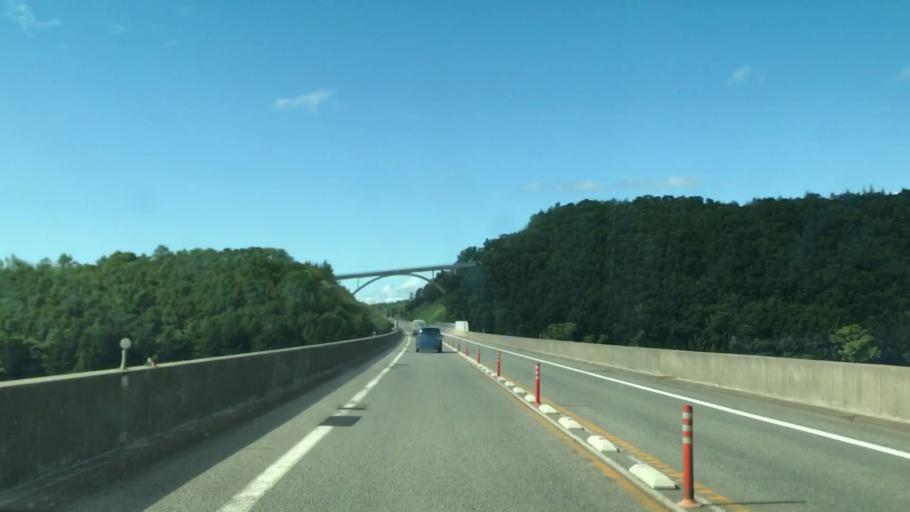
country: JP
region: Hokkaido
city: Date
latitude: 42.4584
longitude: 140.9120
